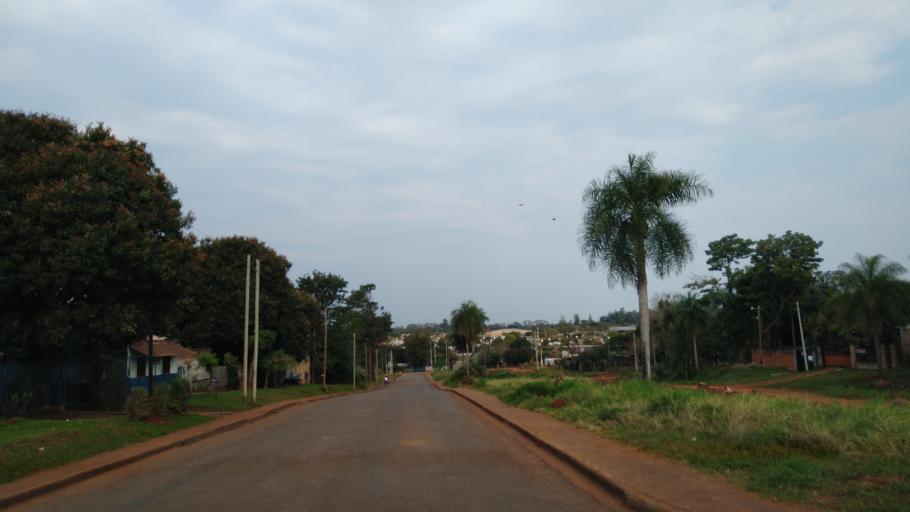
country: AR
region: Misiones
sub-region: Departamento de Capital
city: Posadas
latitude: -27.4296
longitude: -55.8775
